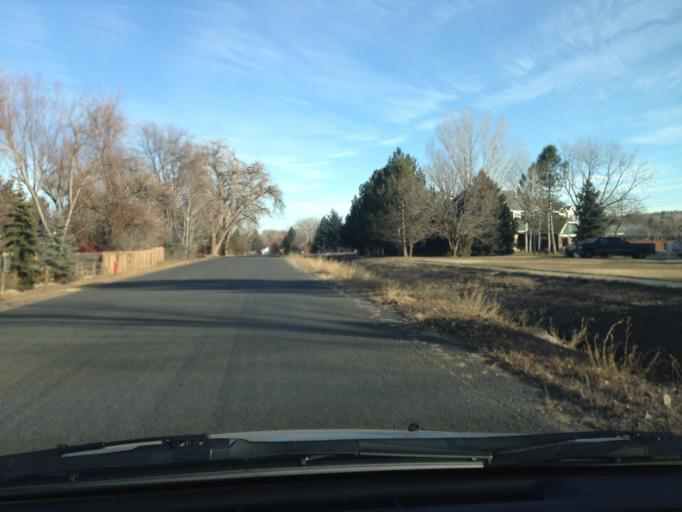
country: US
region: Colorado
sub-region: Boulder County
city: Niwot
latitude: 40.1052
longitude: -105.1639
